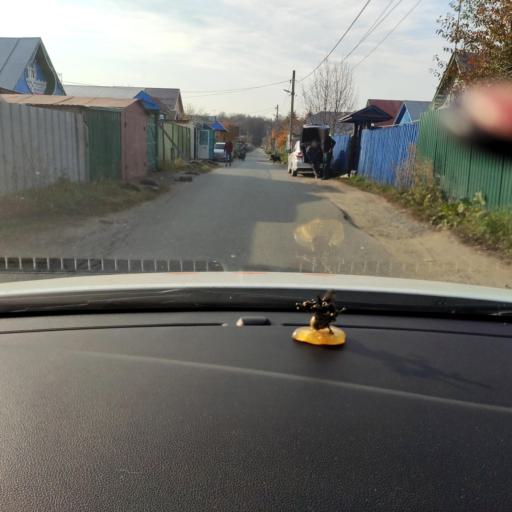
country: RU
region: Tatarstan
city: Osinovo
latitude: 55.8502
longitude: 48.8896
